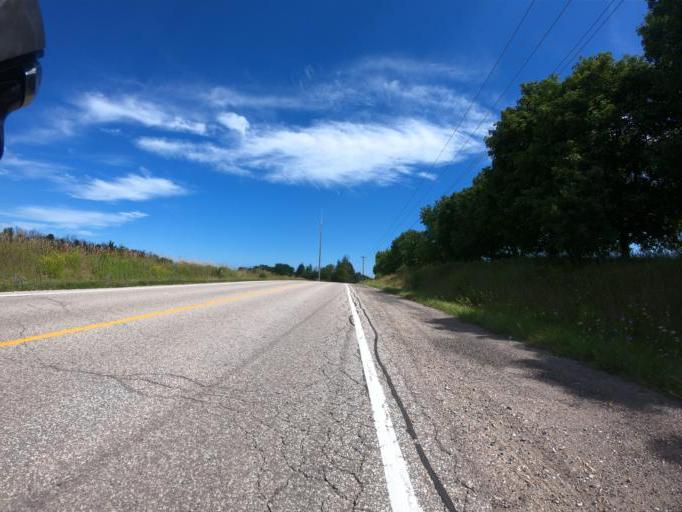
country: CA
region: Ontario
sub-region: Wellington County
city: Guelph
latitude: 43.5439
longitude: -80.3816
